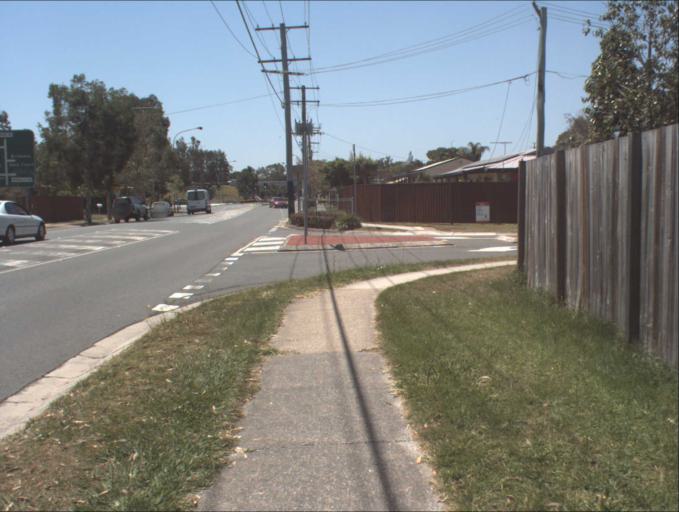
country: AU
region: Queensland
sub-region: Logan
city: Beenleigh
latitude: -27.6874
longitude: 153.1791
